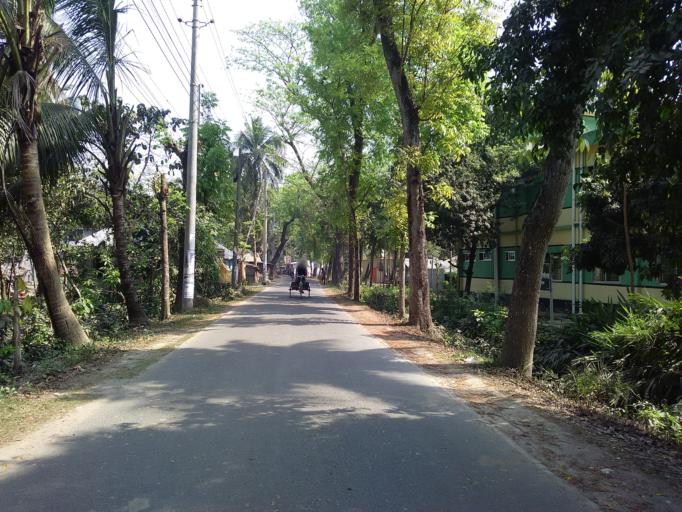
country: BD
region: Khulna
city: Khulna
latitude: 22.8877
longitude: 89.5344
